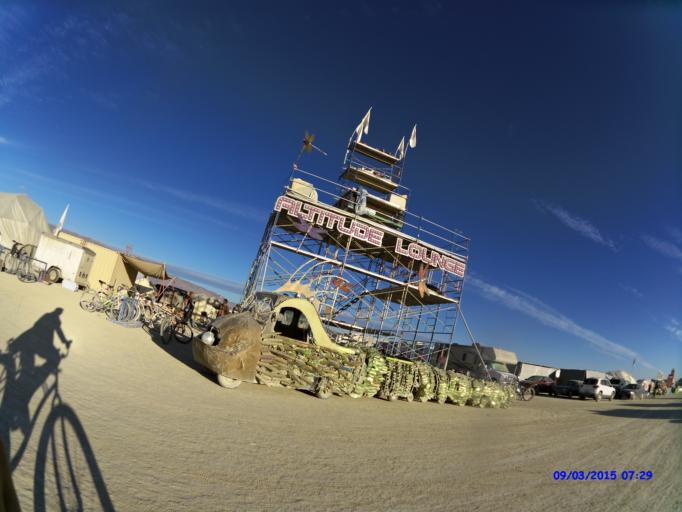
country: US
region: Nevada
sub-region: Pershing County
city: Lovelock
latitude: 40.7899
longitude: -119.2162
